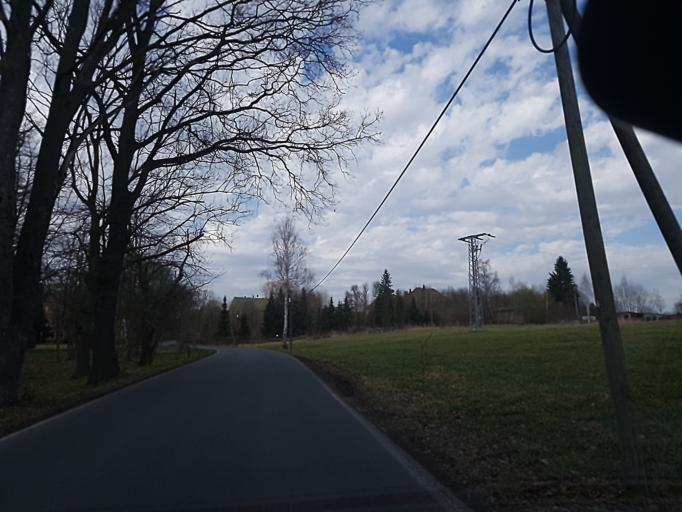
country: DE
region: Saxony
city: Grossweitzschen
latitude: 51.1418
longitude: 13.0357
